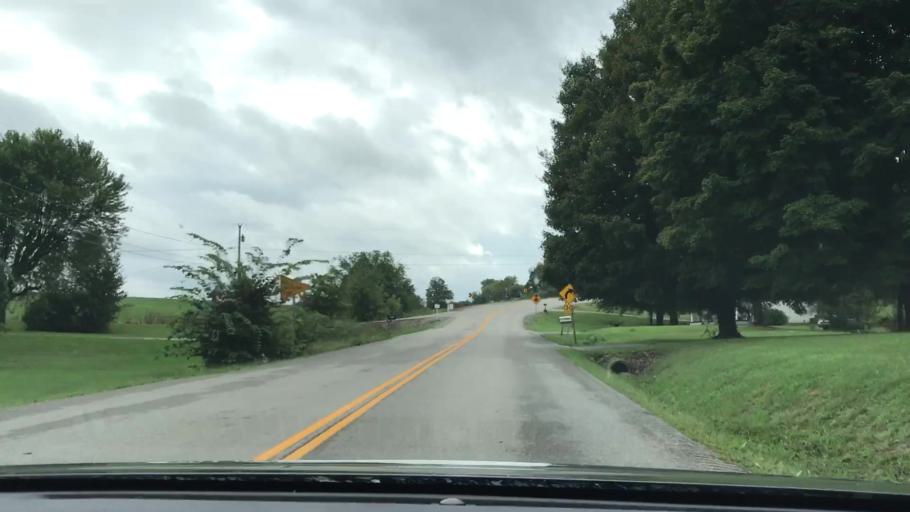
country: US
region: Kentucky
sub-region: Barren County
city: Glasgow
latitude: 36.9590
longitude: -85.8639
